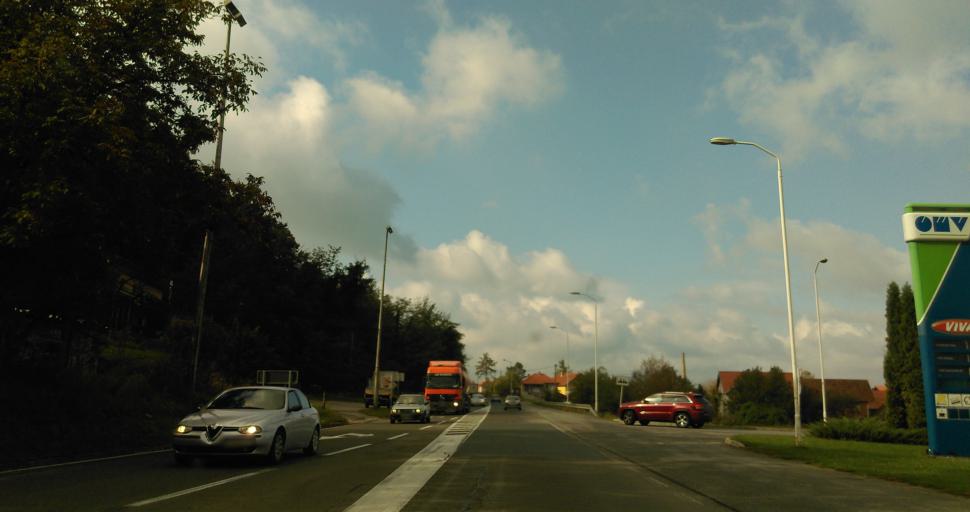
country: RS
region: Central Serbia
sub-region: Kolubarski Okrug
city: Lajkovac
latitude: 44.3651
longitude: 20.1972
